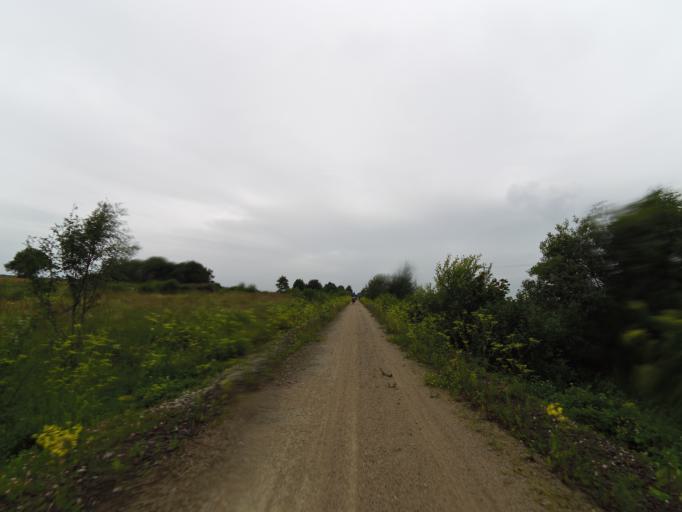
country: EE
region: Laeaene
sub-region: Ridala Parish
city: Uuemoisa
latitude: 58.9540
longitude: 23.8174
